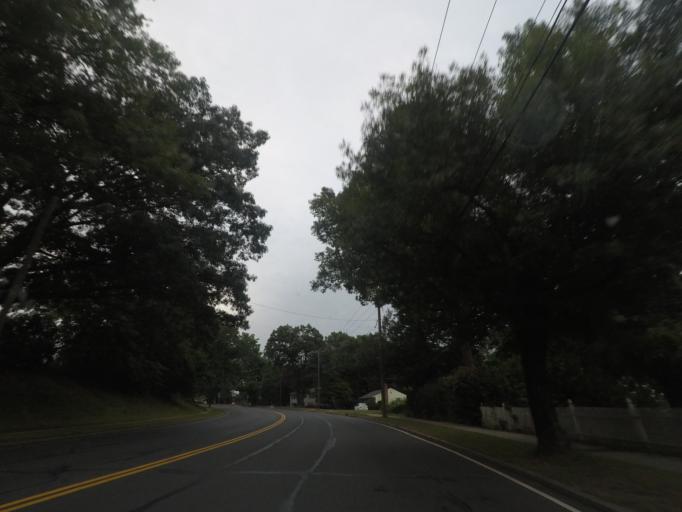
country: US
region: Massachusetts
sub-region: Hampden County
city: Ludlow
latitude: 42.1488
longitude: -72.5081
